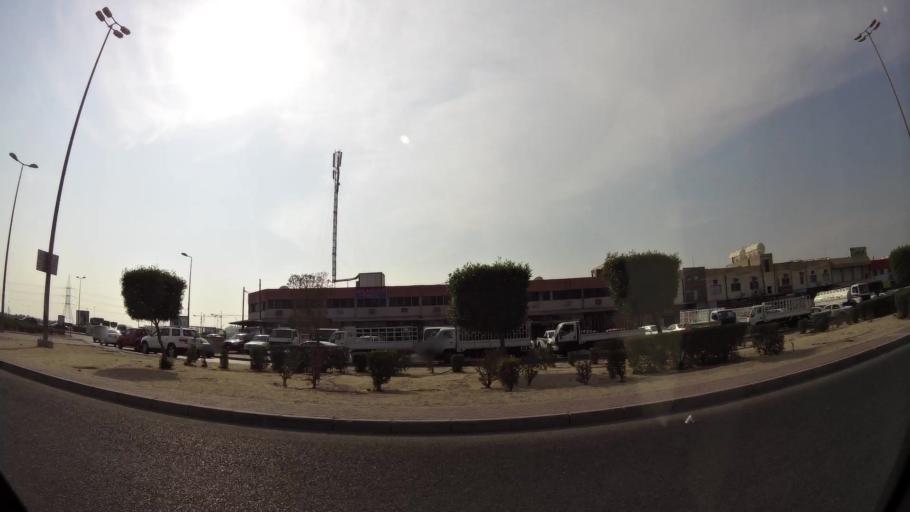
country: KW
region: Al Asimah
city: Ar Rabiyah
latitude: 29.3079
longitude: 47.9487
